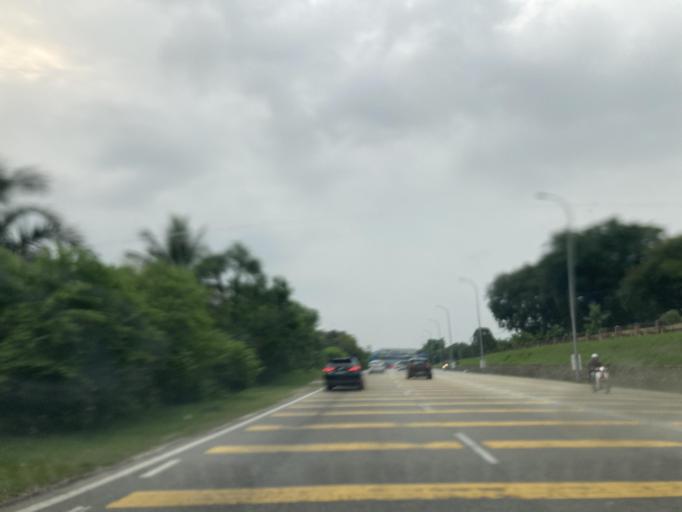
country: MY
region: Selangor
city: Kuang
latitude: 3.2053
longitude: 101.5430
